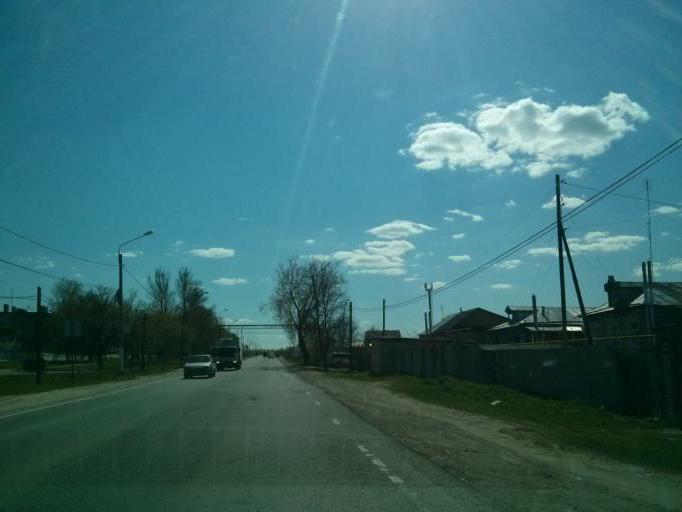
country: RU
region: Nizjnij Novgorod
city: Taremskoye
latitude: 55.9271
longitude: 43.0384
